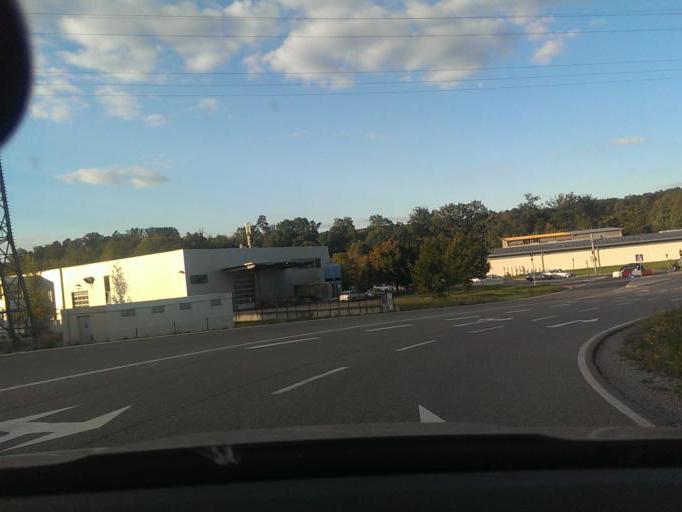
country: DE
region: Baden-Wuerttemberg
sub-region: Karlsruhe Region
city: Ispringen
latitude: 48.9052
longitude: 8.6507
